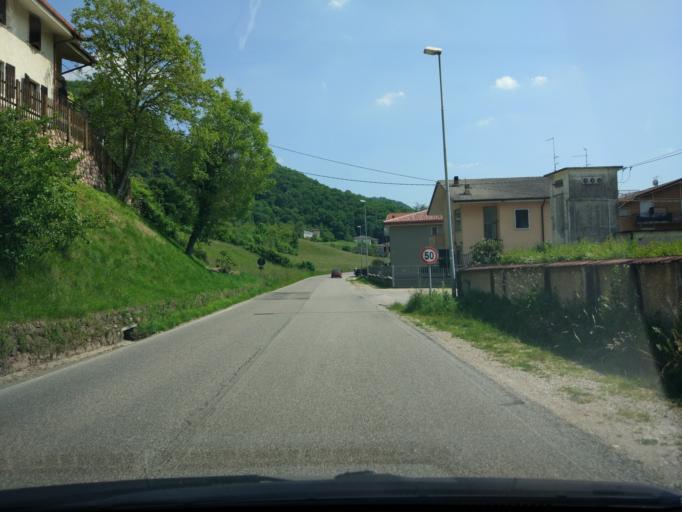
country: IT
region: Veneto
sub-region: Provincia di Verona
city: Badia Calavena
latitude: 45.5714
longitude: 11.1528
